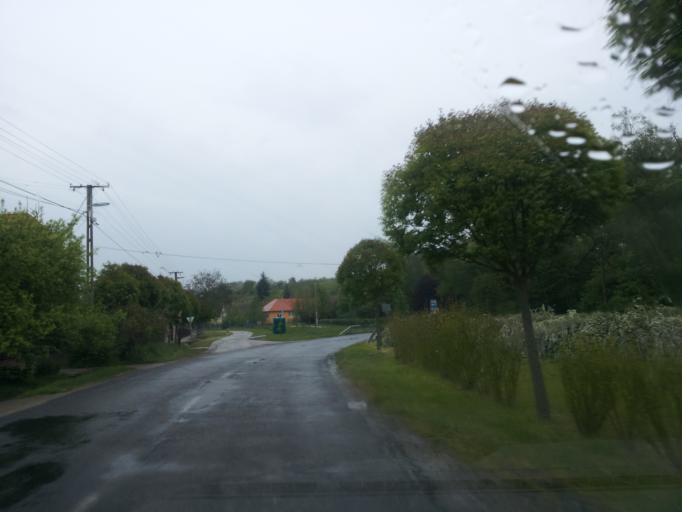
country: HU
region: Tolna
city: Szekszard
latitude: 46.2818
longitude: 18.6441
